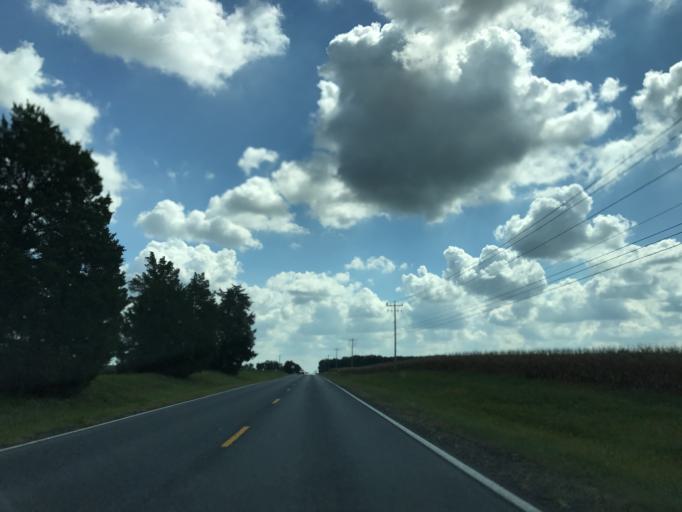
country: US
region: Maryland
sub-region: Queen Anne's County
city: Centreville
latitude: 39.0243
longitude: -76.0165
